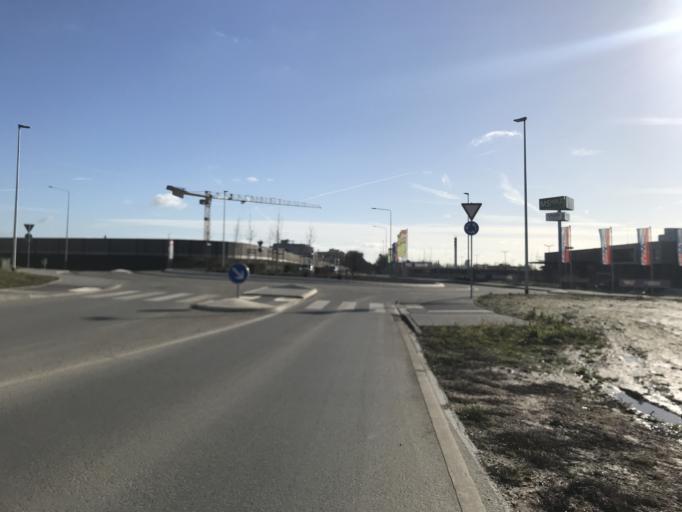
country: DE
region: Hesse
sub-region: Regierungsbezirk Darmstadt
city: Hochheim am Main
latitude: 50.0617
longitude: 8.3289
